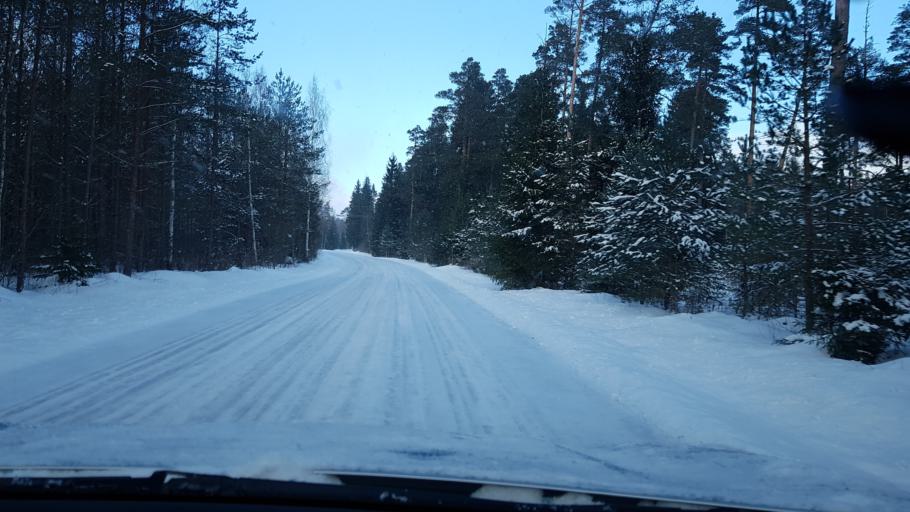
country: EE
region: Harju
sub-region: Nissi vald
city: Turba
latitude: 59.2107
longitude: 24.1414
